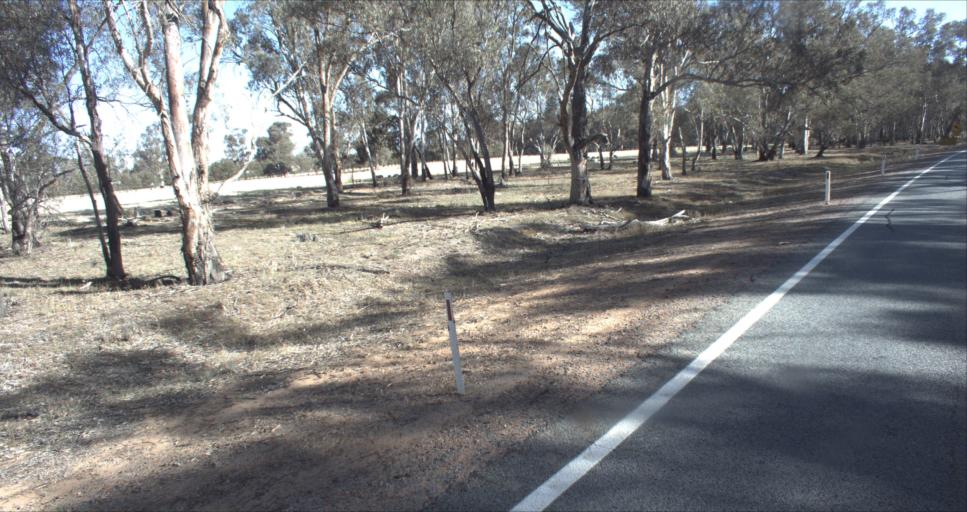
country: AU
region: New South Wales
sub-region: Leeton
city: Leeton
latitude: -34.6299
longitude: 146.3764
